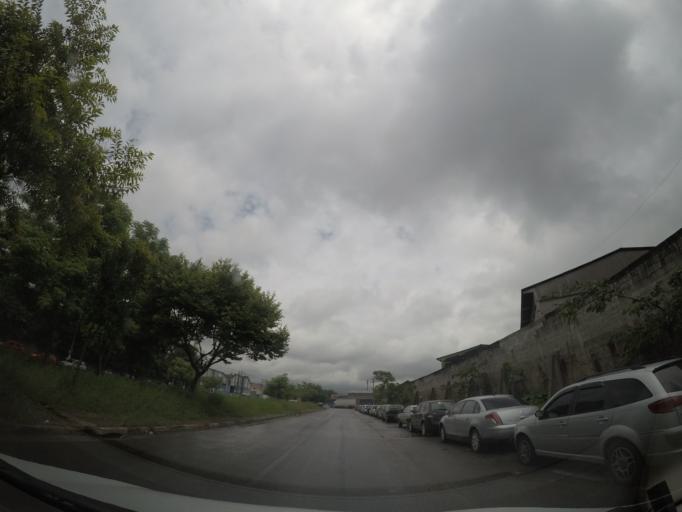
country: BR
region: Sao Paulo
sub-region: Guarulhos
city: Guarulhos
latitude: -23.4649
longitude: -46.4841
